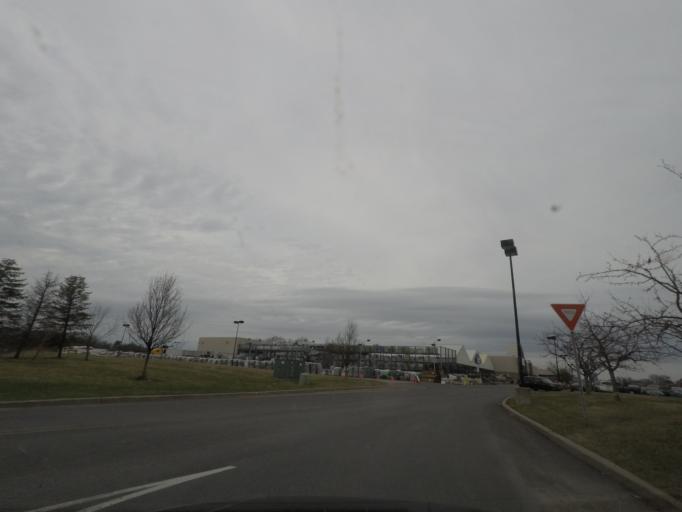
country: US
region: New York
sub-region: Albany County
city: Delmar
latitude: 42.6101
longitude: -73.7906
